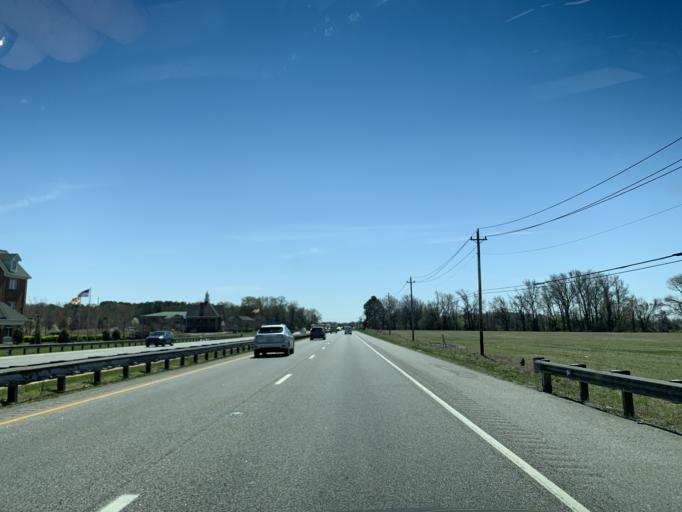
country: US
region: Maryland
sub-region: Talbot County
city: Easton
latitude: 38.7892
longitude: -76.0603
